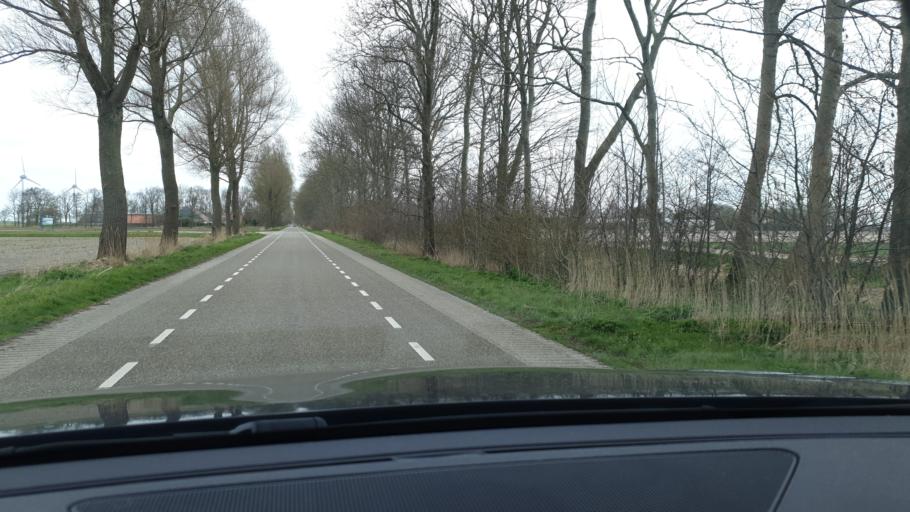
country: NL
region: Friesland
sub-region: Gemeente Lemsterland
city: Lemmer
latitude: 52.7880
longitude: 5.6347
